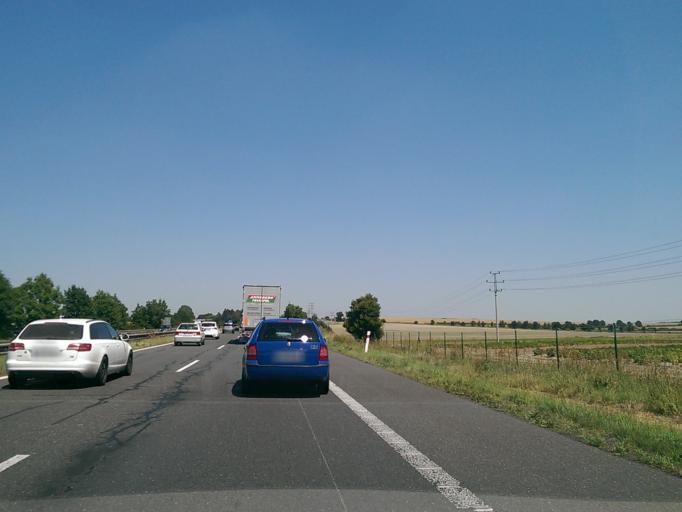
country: CZ
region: Central Bohemia
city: Benatky nad Jizerou
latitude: 50.2759
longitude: 14.8228
